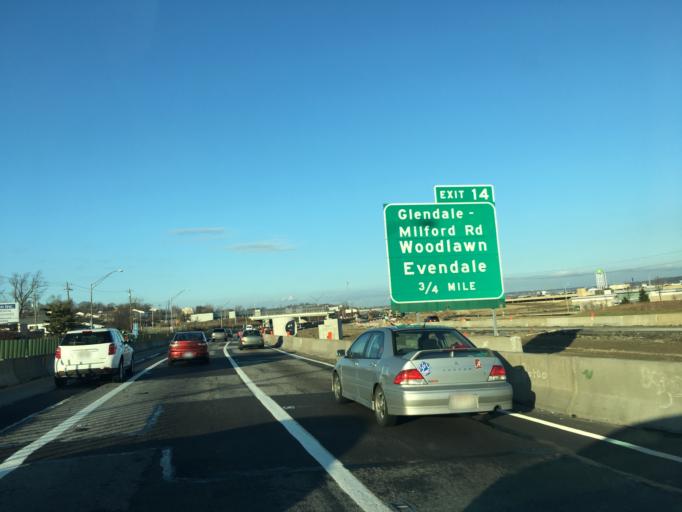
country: US
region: Ohio
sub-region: Hamilton County
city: Lincoln Heights
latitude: 39.2393
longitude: -84.4513
